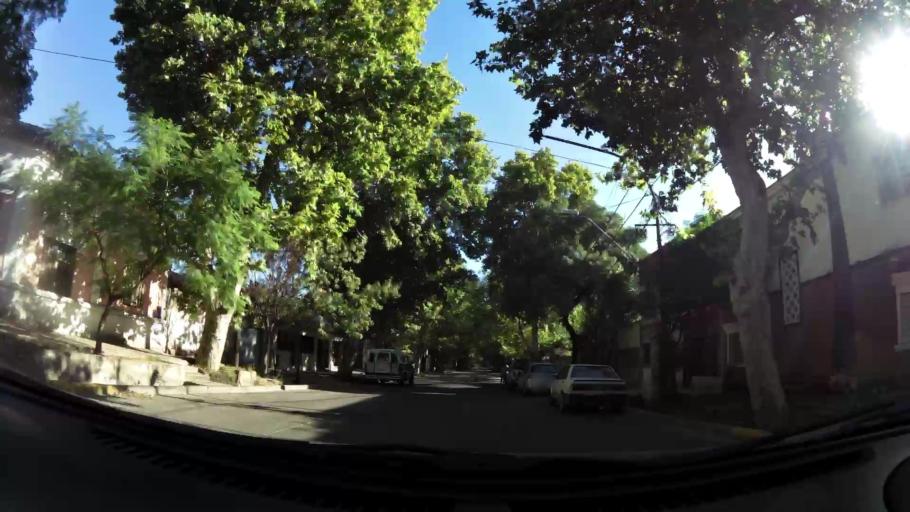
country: AR
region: Mendoza
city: Las Heras
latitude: -32.8687
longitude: -68.8363
